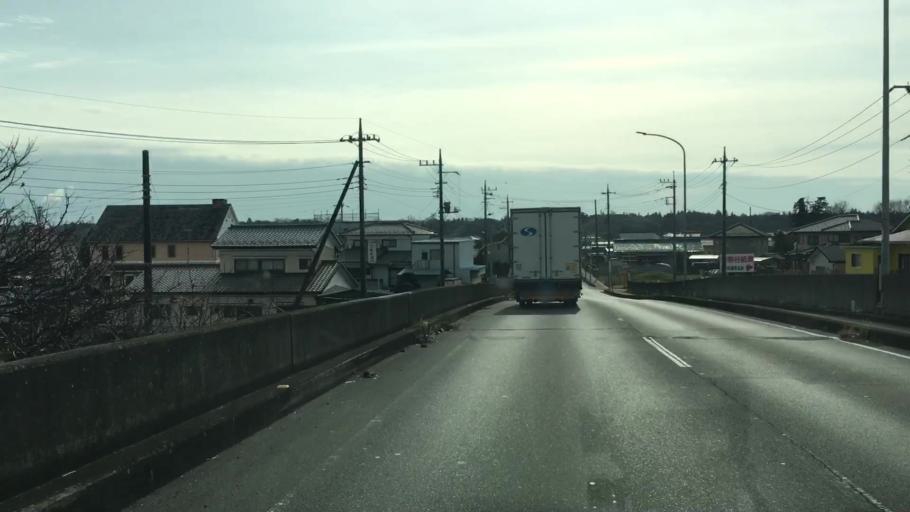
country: JP
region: Saitama
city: Kumagaya
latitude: 36.1338
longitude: 139.3236
